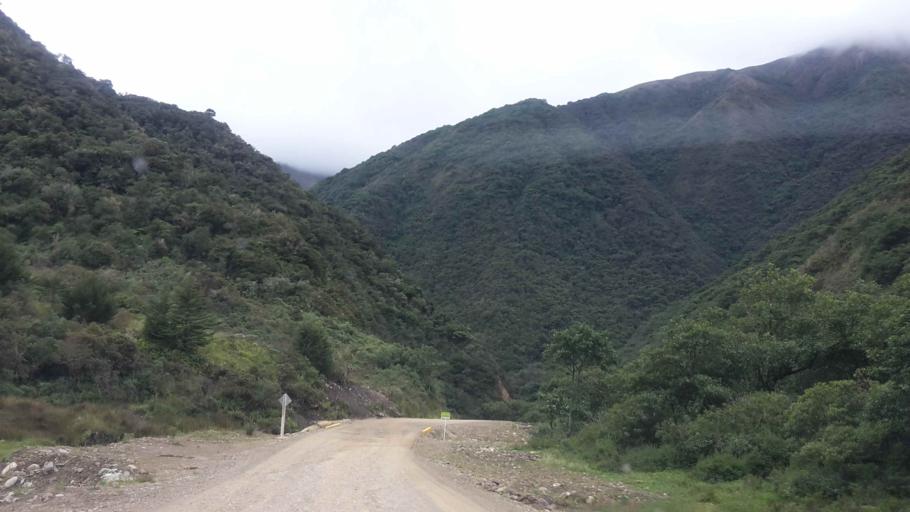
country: BO
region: Cochabamba
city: Totora
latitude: -17.5612
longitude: -65.2739
